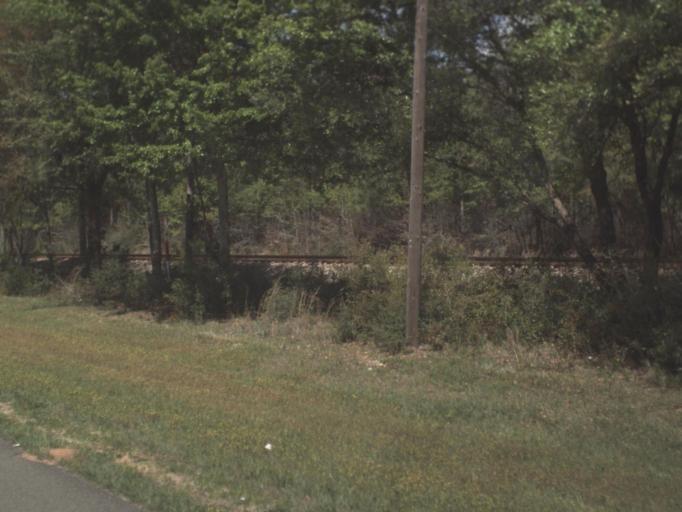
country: US
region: Florida
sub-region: Santa Rosa County
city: East Milton
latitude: 30.6461
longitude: -86.9234
